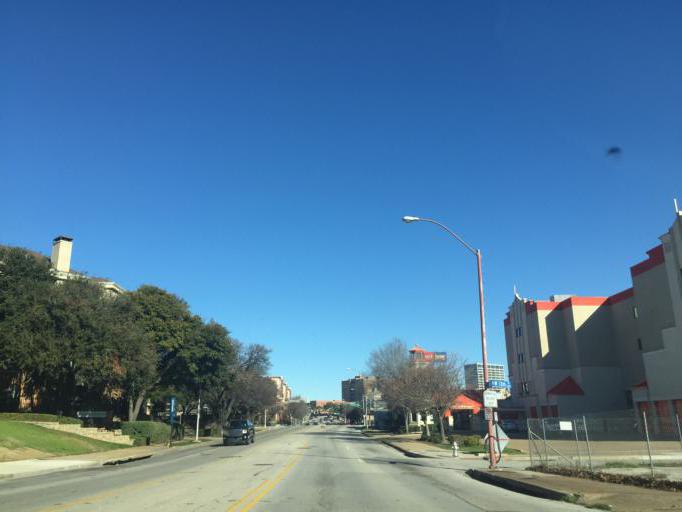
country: US
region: Texas
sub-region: Tarrant County
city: Fort Worth
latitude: 32.7475
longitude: -97.3374
